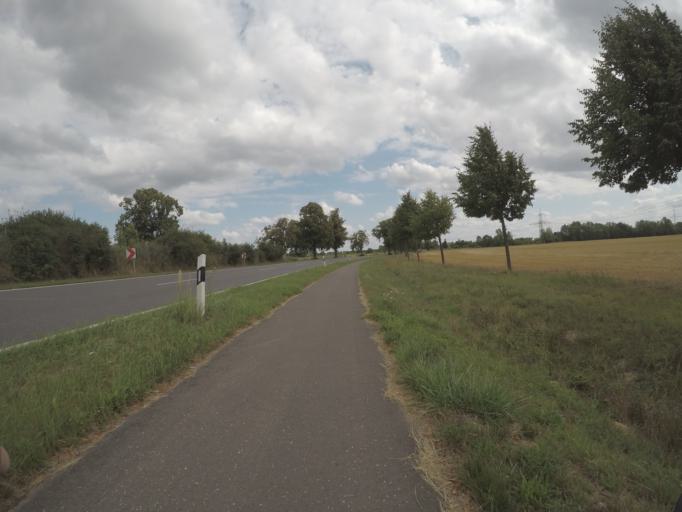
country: DE
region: Brandenburg
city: Wustermark
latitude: 52.5573
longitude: 12.9295
